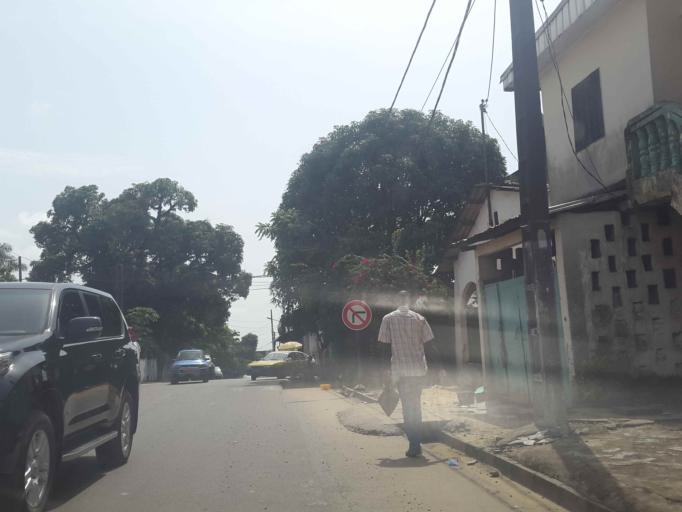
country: CM
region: Littoral
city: Douala
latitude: 4.0700
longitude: 9.7146
